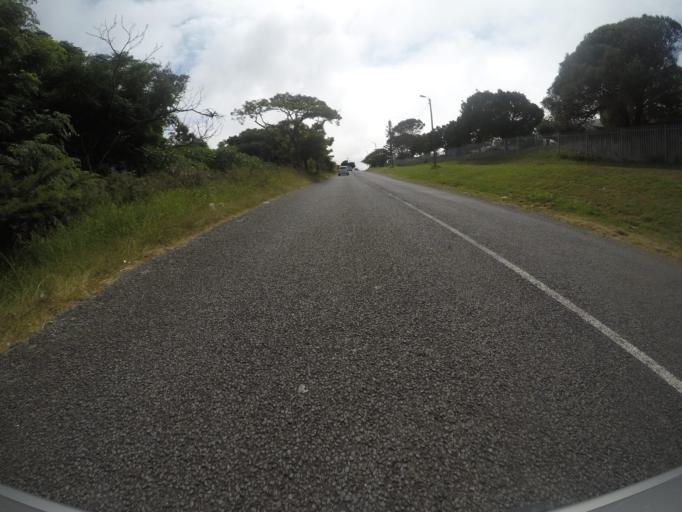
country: ZA
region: Eastern Cape
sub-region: Buffalo City Metropolitan Municipality
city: East London
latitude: -32.9961
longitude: 27.9115
